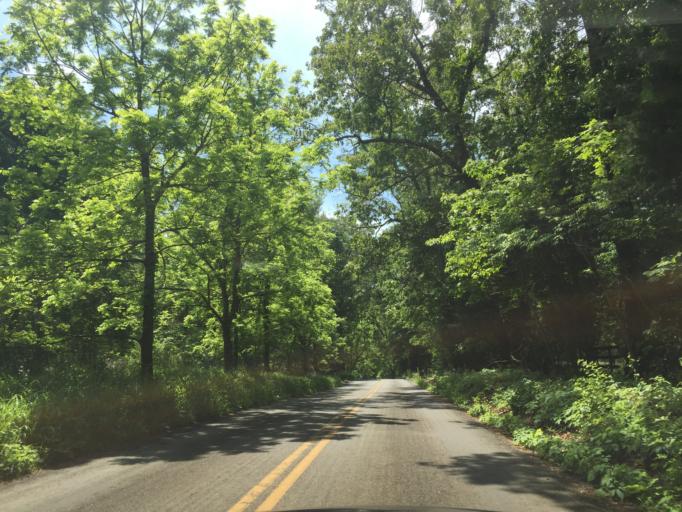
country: US
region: Virginia
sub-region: Warren County
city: Apple Mountain Lake
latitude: 38.9684
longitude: -78.1231
